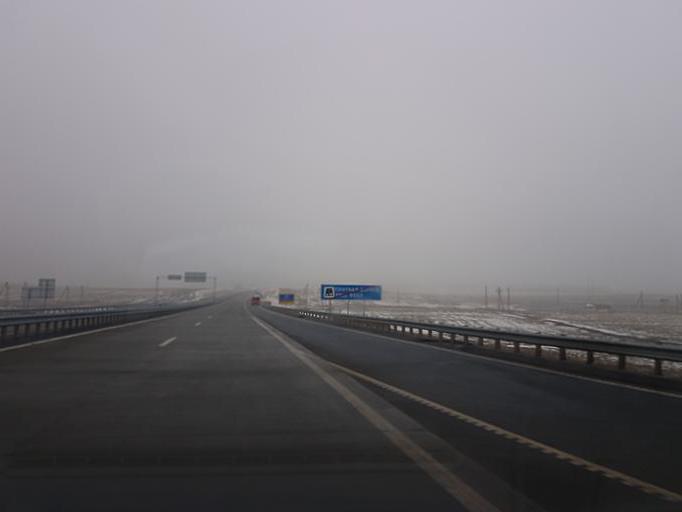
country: BY
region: Minsk
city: Samakhvalavichy
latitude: 53.7069
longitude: 27.4430
